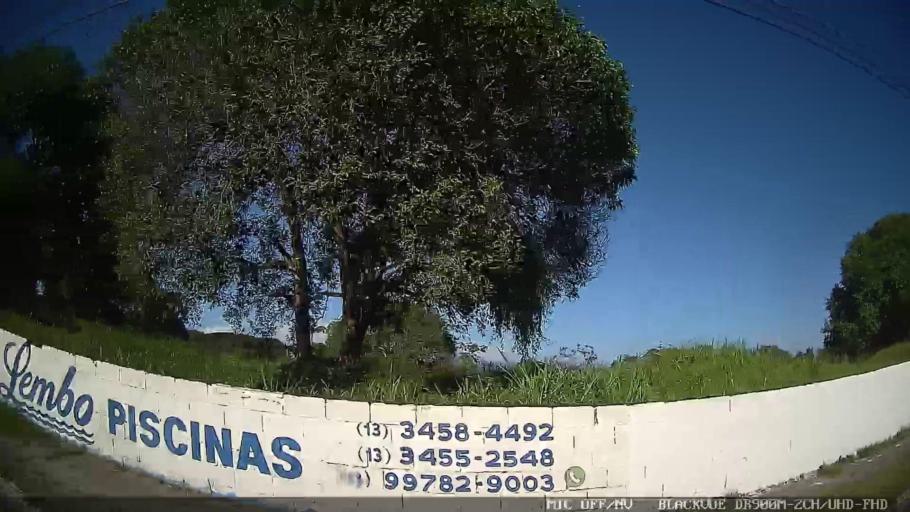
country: BR
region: Sao Paulo
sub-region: Peruibe
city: Peruibe
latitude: -24.2735
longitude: -46.9537
